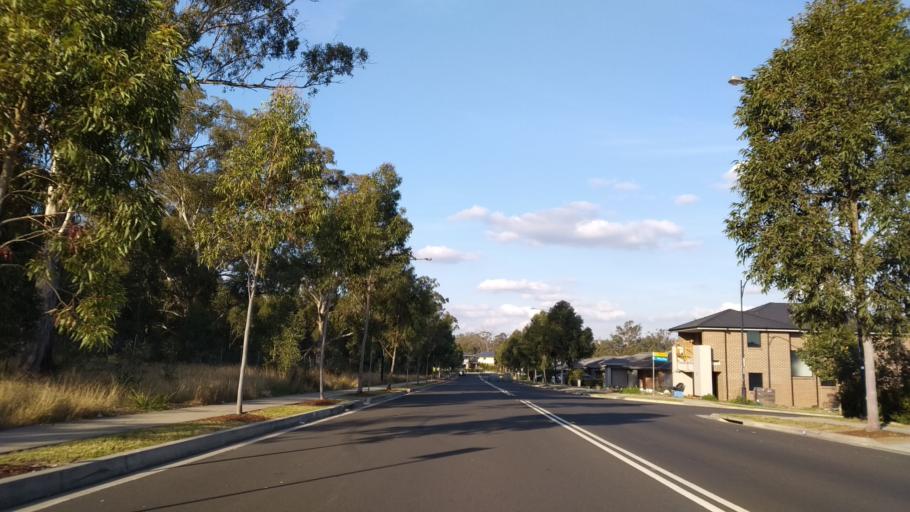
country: AU
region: New South Wales
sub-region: Penrith Municipality
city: Werrington Downs
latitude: -33.7226
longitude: 150.7328
